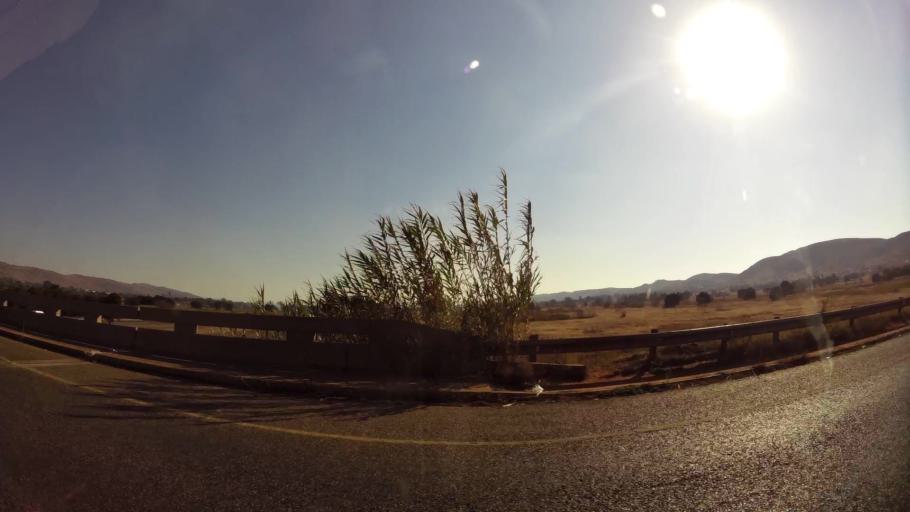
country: ZA
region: Gauteng
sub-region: City of Tshwane Metropolitan Municipality
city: Pretoria
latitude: -25.7033
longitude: 28.1381
